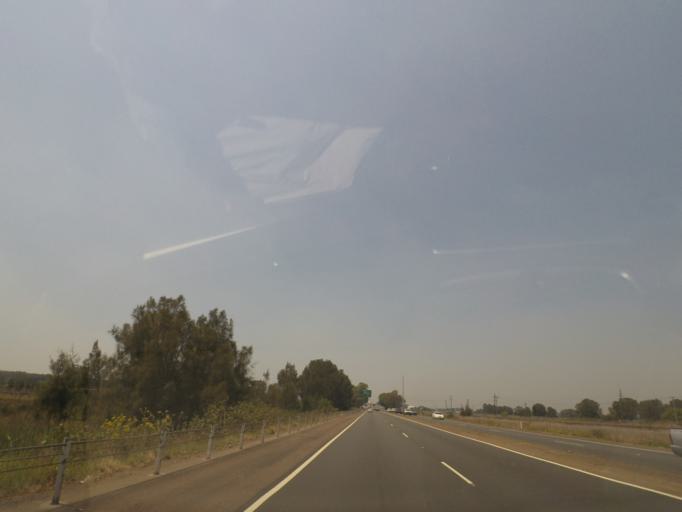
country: AU
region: New South Wales
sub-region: Newcastle
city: Beresfield
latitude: -32.8150
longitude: 151.6775
